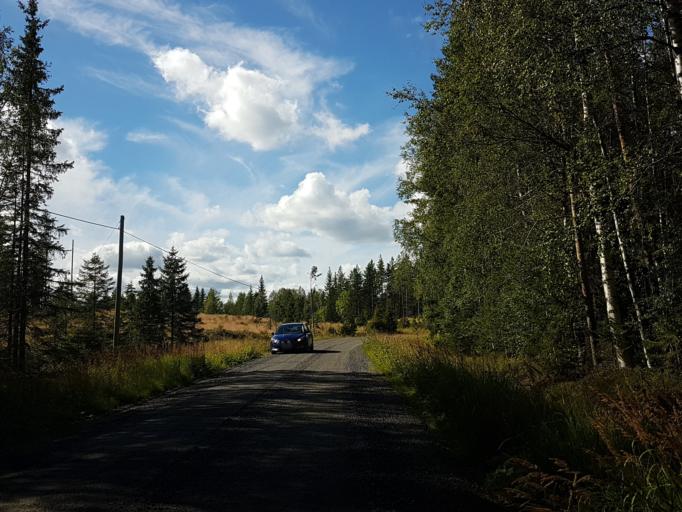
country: SE
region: Vaesterbotten
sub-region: Skelleftea Kommun
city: Burtraesk
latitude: 64.2795
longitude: 20.4722
